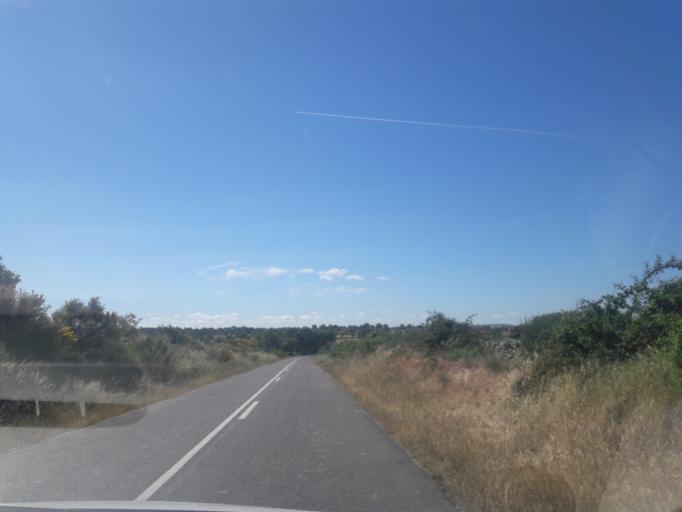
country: ES
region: Castille and Leon
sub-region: Provincia de Salamanca
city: Lumbrales
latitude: 40.9634
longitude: -6.7245
